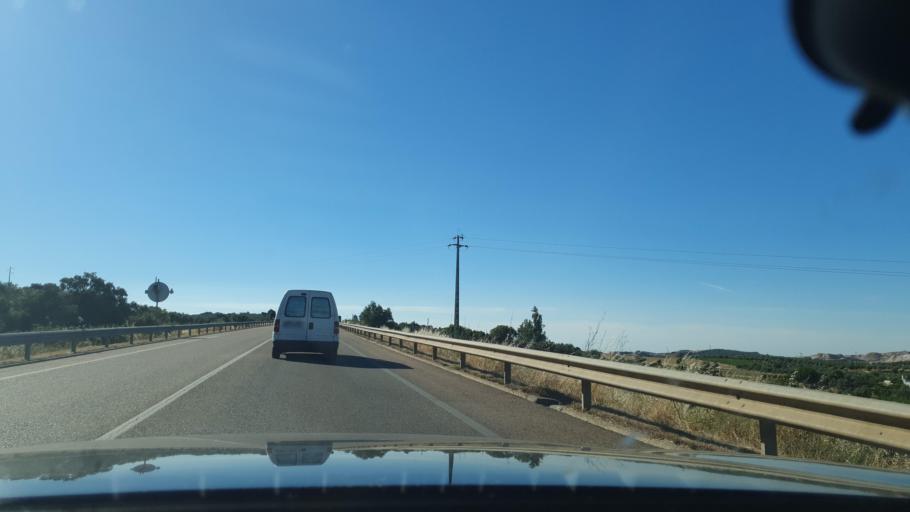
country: PT
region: Evora
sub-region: Vila Vicosa
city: Vila Vicosa
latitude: 38.7719
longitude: -7.4326
